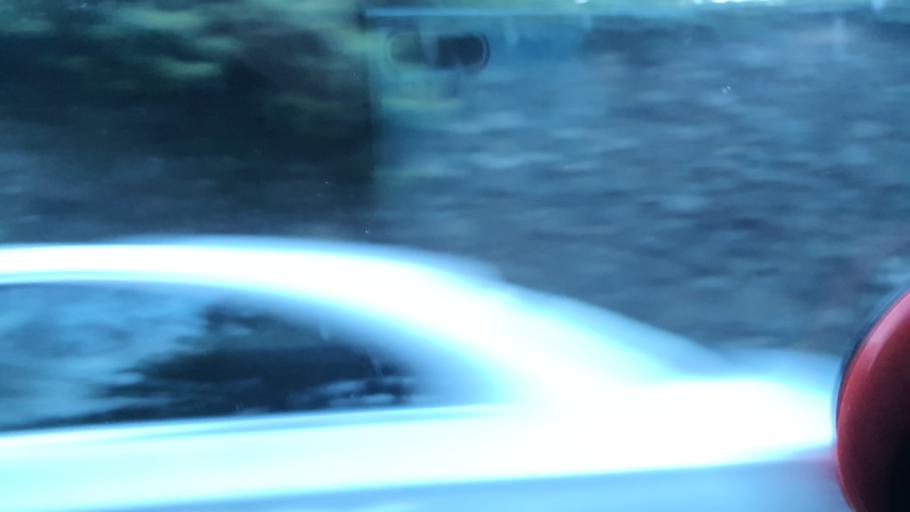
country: GB
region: Northern Ireland
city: Rostrevor
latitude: 54.0987
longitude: -6.1947
